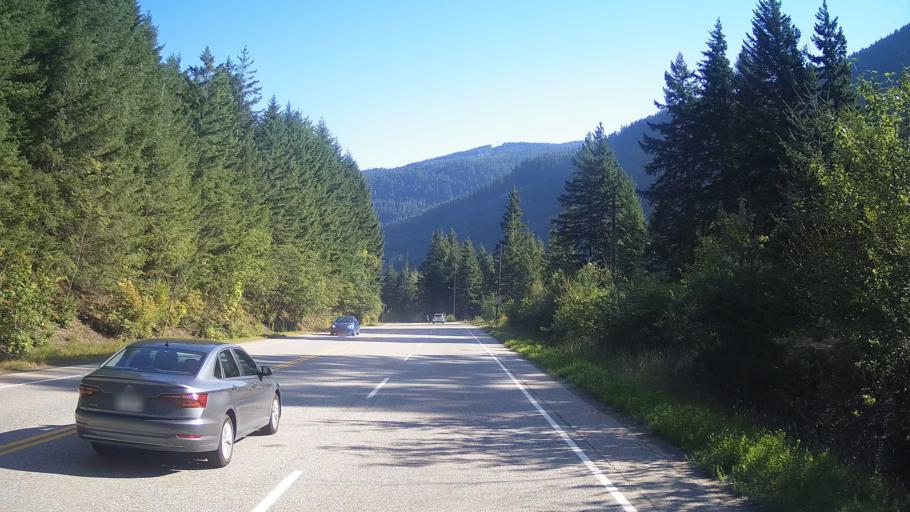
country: CA
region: British Columbia
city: Hope
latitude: 49.6471
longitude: -121.4098
